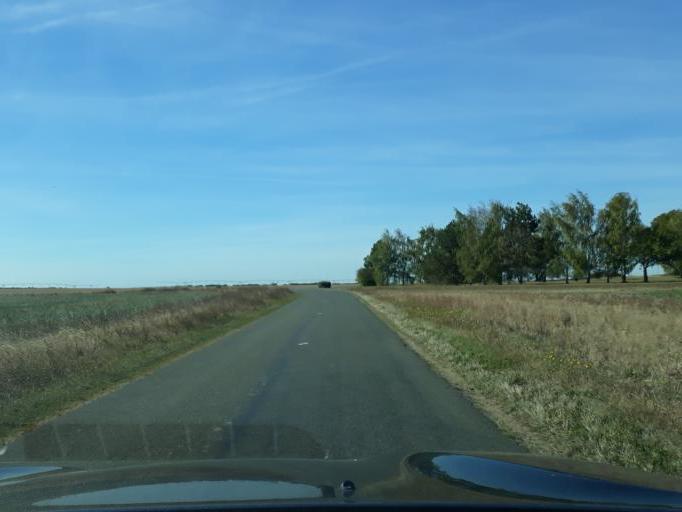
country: FR
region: Centre
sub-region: Departement du Loir-et-Cher
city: Ouzouer-le-Marche
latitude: 47.8683
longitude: 1.5544
